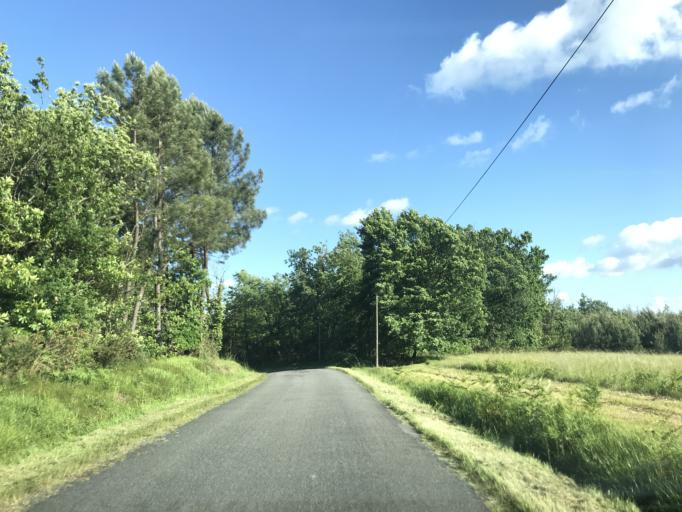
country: FR
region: Poitou-Charentes
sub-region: Departement de la Charente
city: Chalais
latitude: 45.2770
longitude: -0.0374
